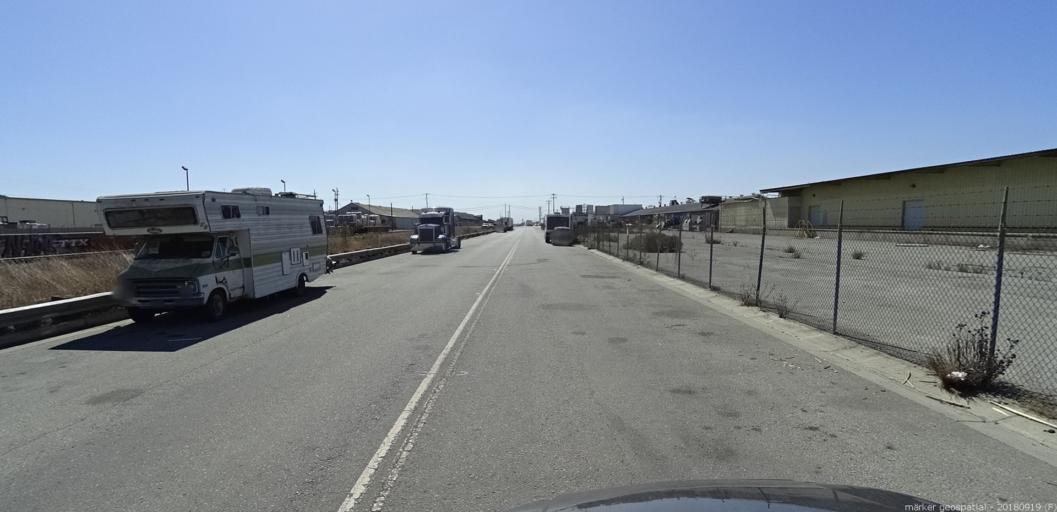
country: US
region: California
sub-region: Monterey County
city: Castroville
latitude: 36.7601
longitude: -121.7448
